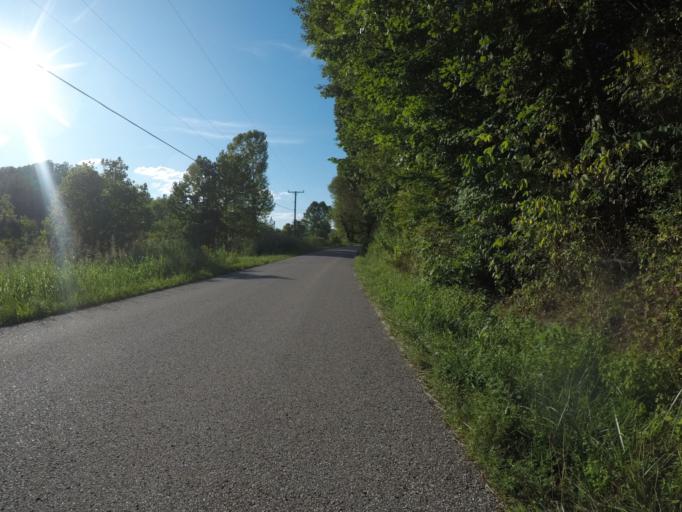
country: US
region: West Virginia
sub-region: Cabell County
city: Huntington
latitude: 38.5099
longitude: -82.4943
